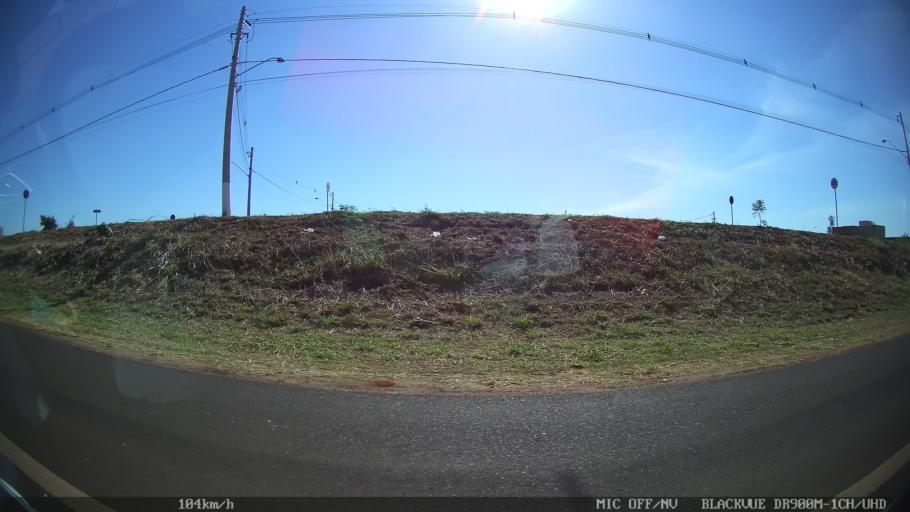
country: BR
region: Sao Paulo
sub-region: Olimpia
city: Olimpia
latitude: -20.7301
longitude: -48.8693
